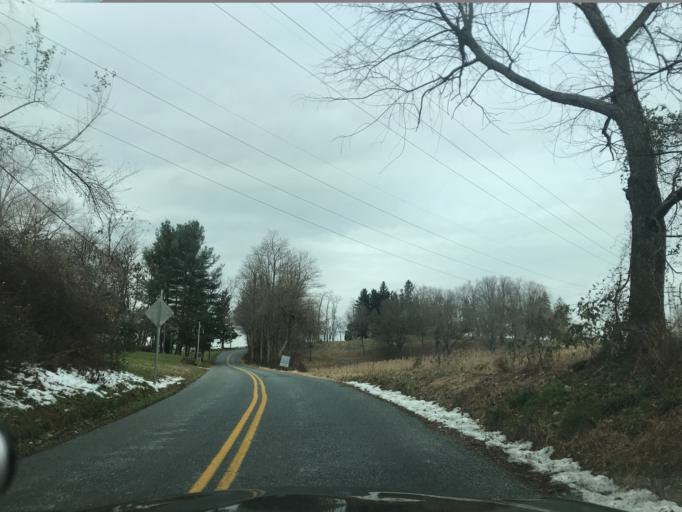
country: US
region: Maryland
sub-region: Harford County
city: Jarrettsville
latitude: 39.6659
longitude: -76.4314
